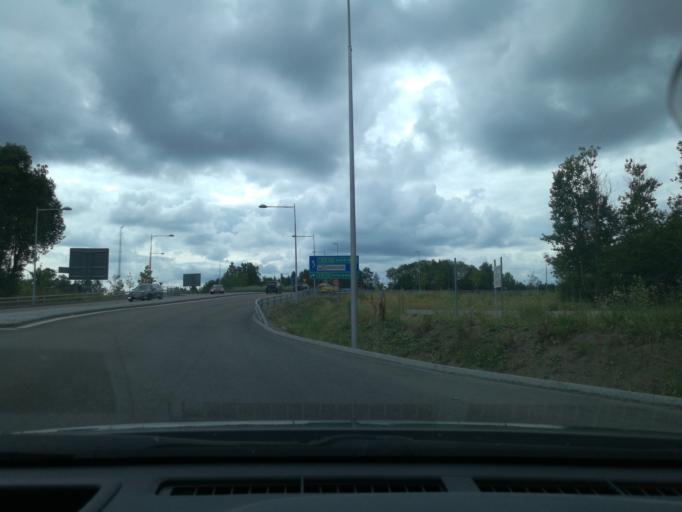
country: SE
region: Stockholm
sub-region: Taby Kommun
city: Taby
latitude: 59.4450
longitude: 18.0959
